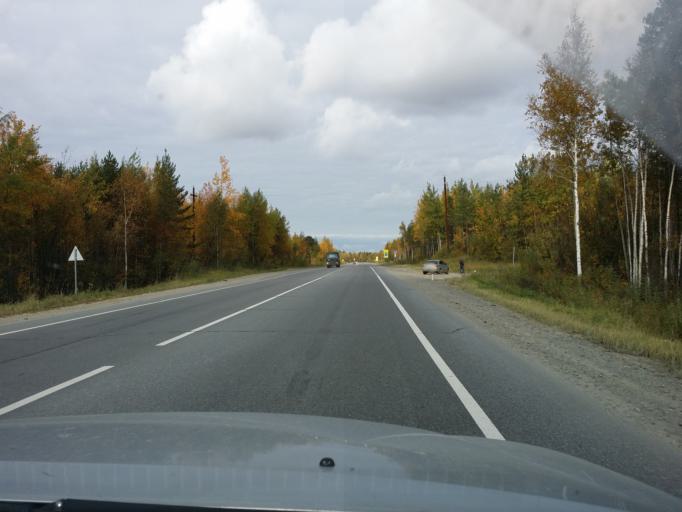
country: RU
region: Khanty-Mansiyskiy Avtonomnyy Okrug
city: Megion
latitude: 61.1063
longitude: 76.0426
